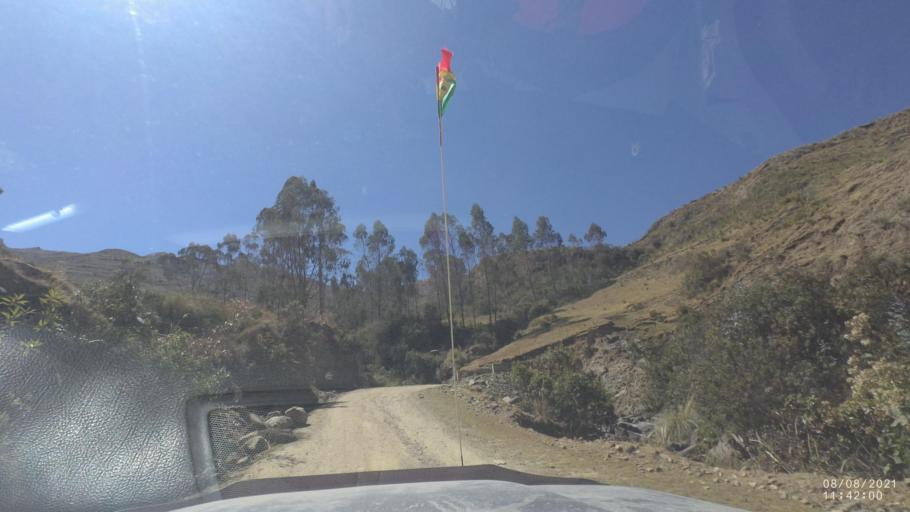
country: BO
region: Cochabamba
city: Colchani
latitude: -16.7957
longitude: -66.6390
